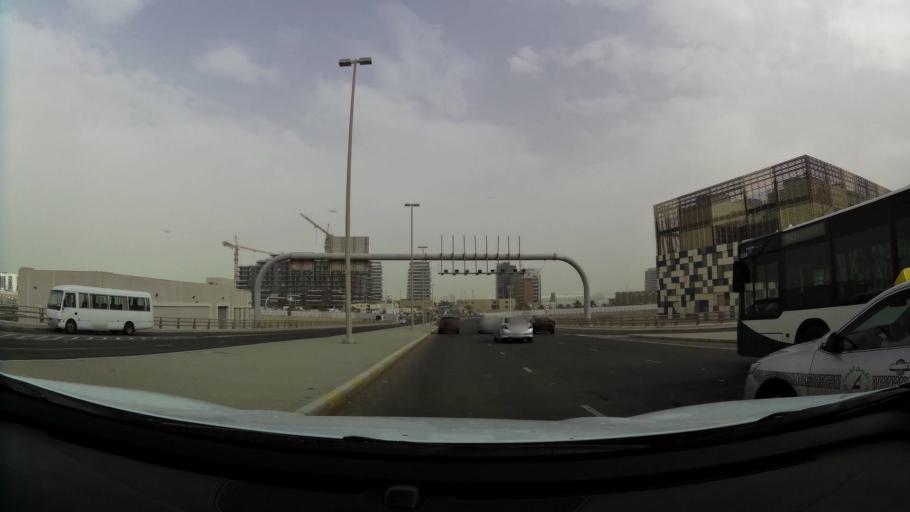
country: AE
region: Abu Dhabi
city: Abu Dhabi
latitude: 24.4462
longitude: 54.6009
